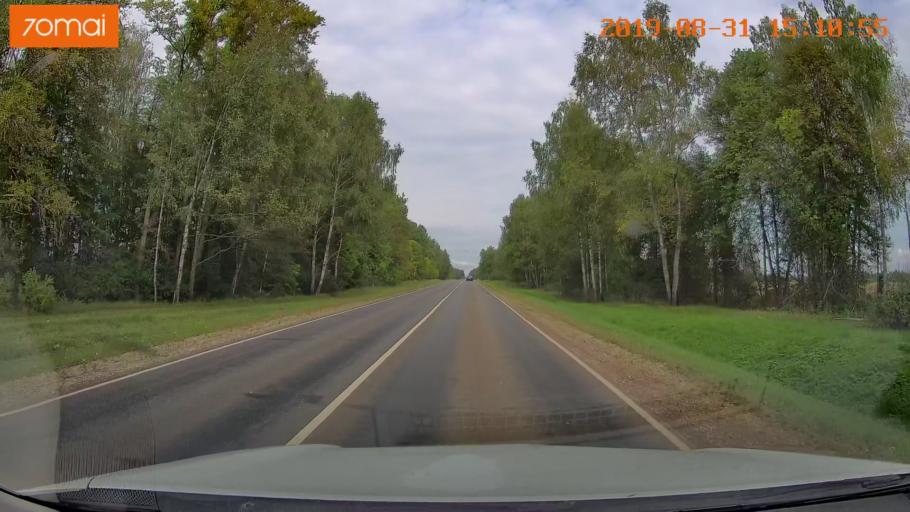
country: RU
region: Kaluga
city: Spas-Demensk
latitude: 54.4181
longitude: 34.2311
